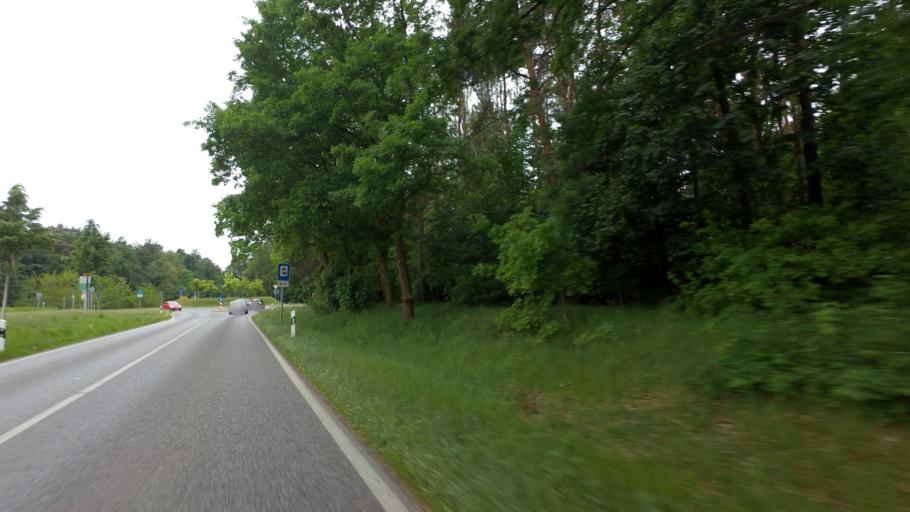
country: DE
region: Brandenburg
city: Wandlitz
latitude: 52.7688
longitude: 13.4760
